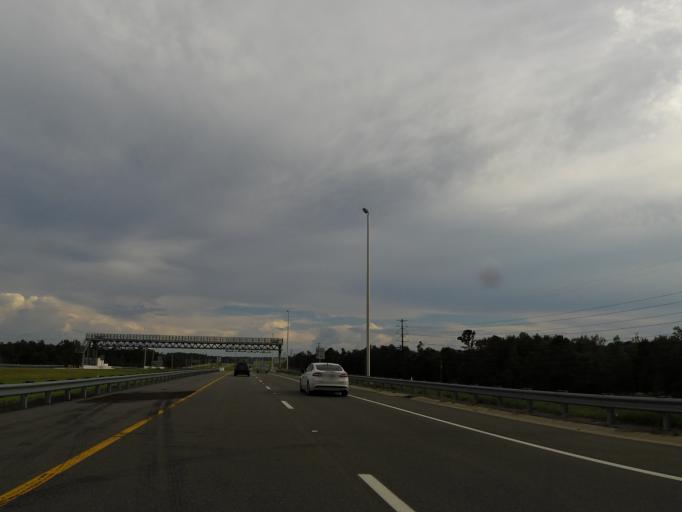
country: US
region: Florida
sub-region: Clay County
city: Lakeside
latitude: 30.1317
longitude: -81.8308
